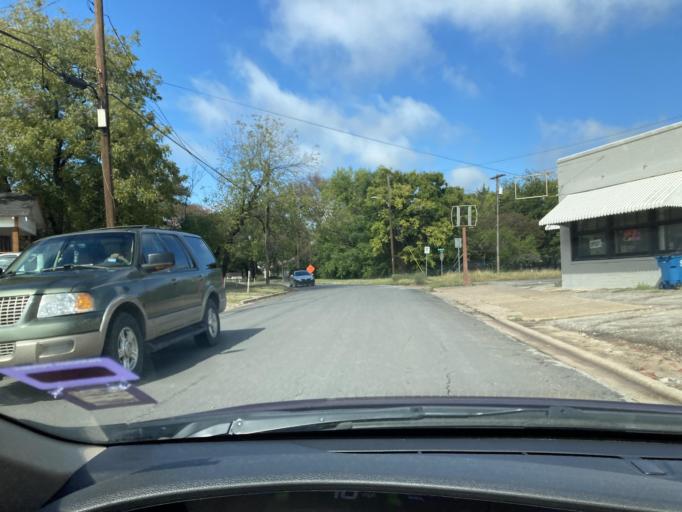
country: US
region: Texas
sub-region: Navarro County
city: Corsicana
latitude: 32.0889
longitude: -96.4739
